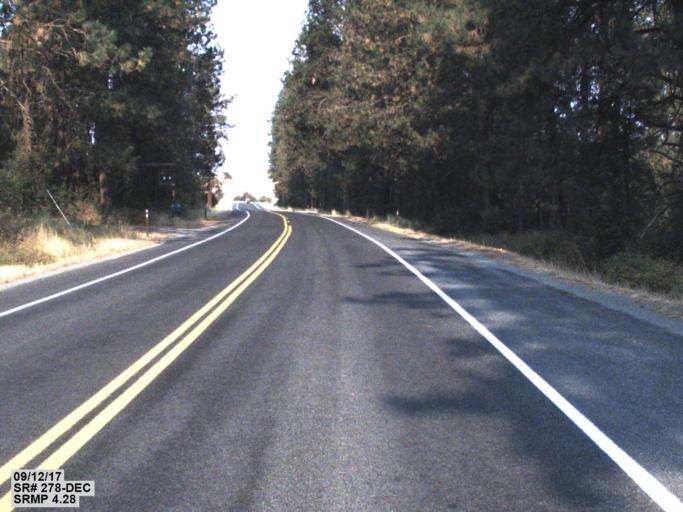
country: US
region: Idaho
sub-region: Benewah County
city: Plummer
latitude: 47.4415
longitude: -117.0633
